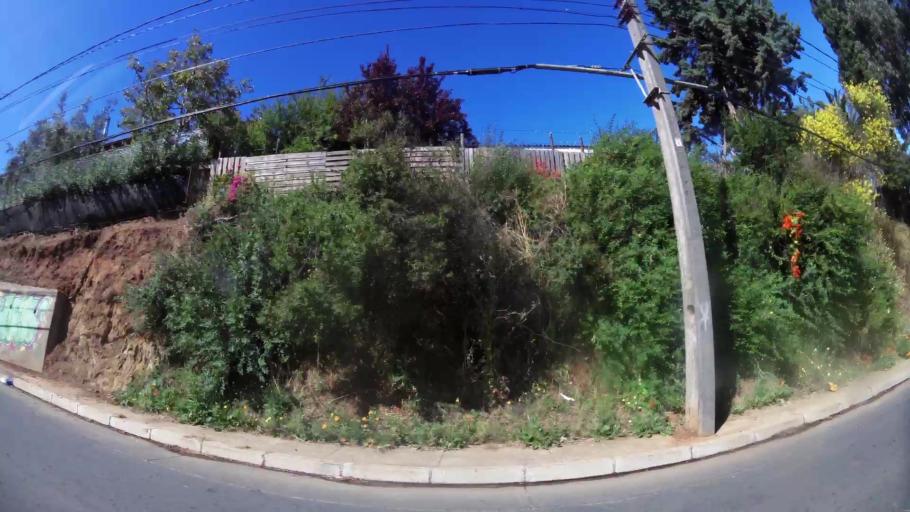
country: CL
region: Valparaiso
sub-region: Provincia de Valparaiso
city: Vina del Mar
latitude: -33.0621
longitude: -71.5762
